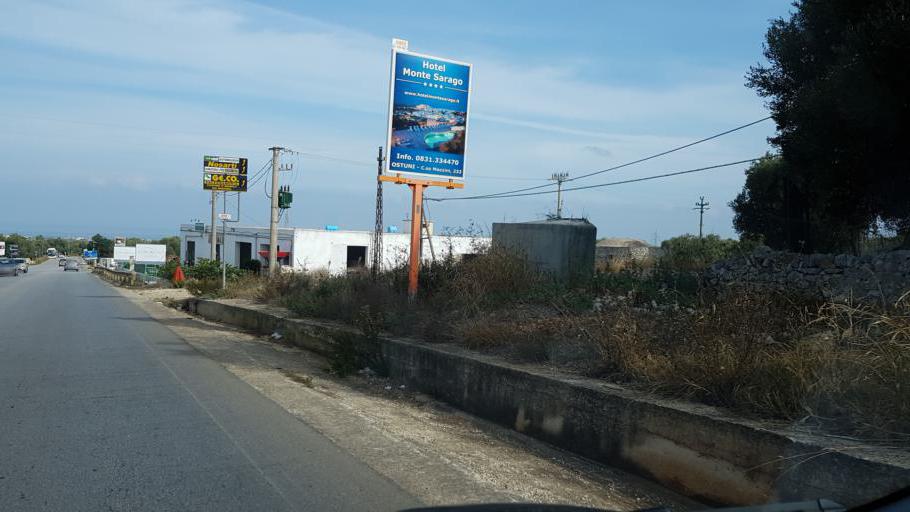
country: IT
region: Apulia
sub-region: Provincia di Brindisi
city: Ostuni
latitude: 40.7409
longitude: 17.5781
